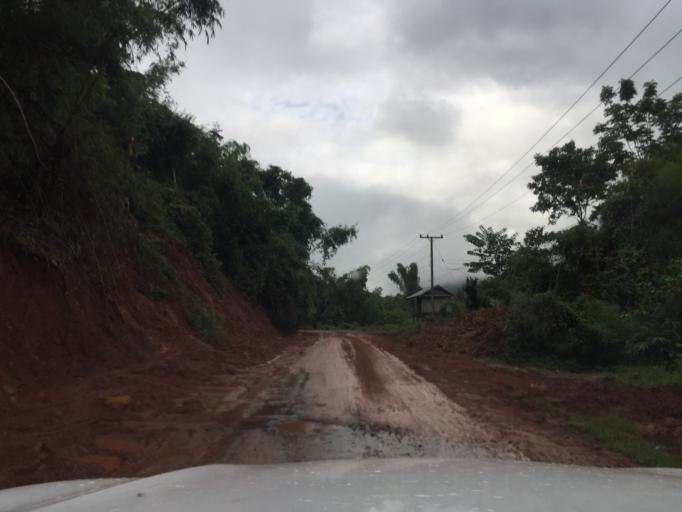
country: LA
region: Oudomxai
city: Muang La
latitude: 20.8428
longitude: 102.1047
